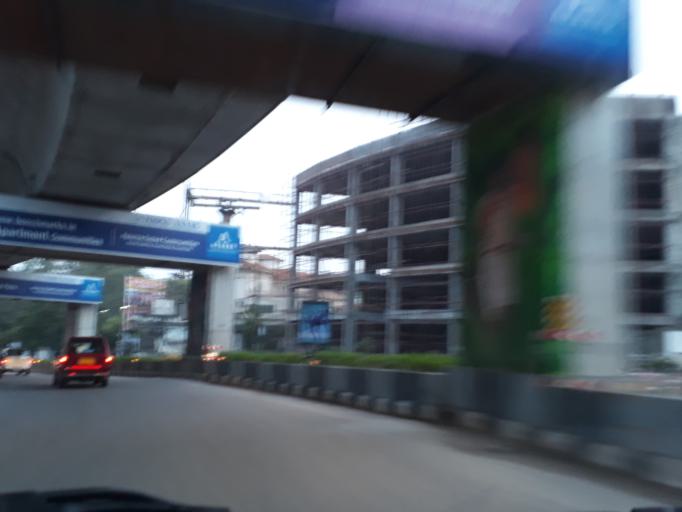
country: IN
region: Telangana
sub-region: Rangareddi
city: Kukatpalli
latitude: 17.4298
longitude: 78.4118
